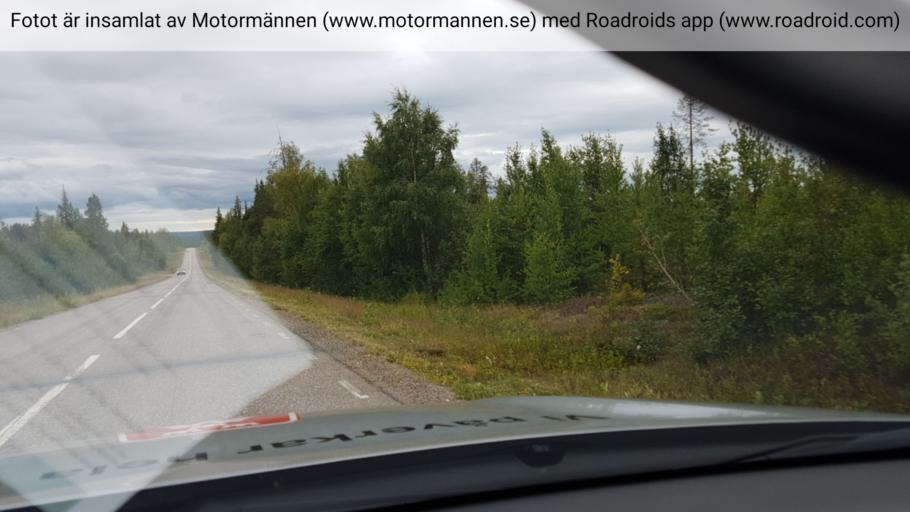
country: SE
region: Norrbotten
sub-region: Overkalix Kommun
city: OEverkalix
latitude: 66.8204
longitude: 23.0151
